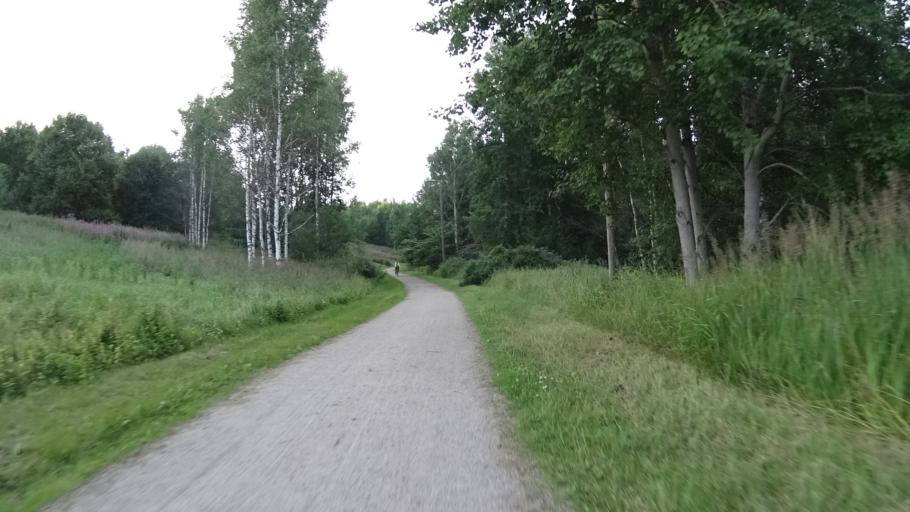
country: FI
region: Uusimaa
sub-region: Helsinki
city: Teekkarikylae
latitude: 60.2106
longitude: 24.8495
